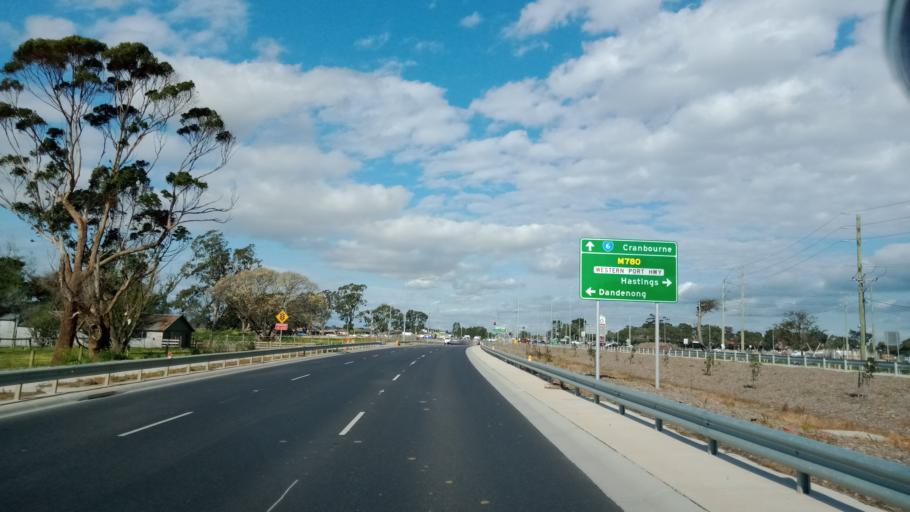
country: AU
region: Victoria
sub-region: Frankston
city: Sandhurst
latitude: -38.0770
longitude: 145.2363
